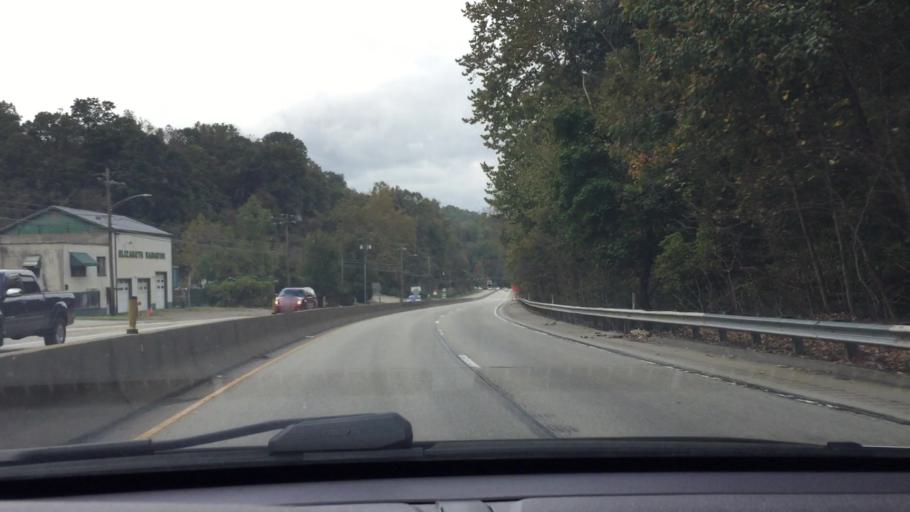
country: US
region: Pennsylvania
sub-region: Allegheny County
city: Elizabeth
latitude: 40.2496
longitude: -79.8775
